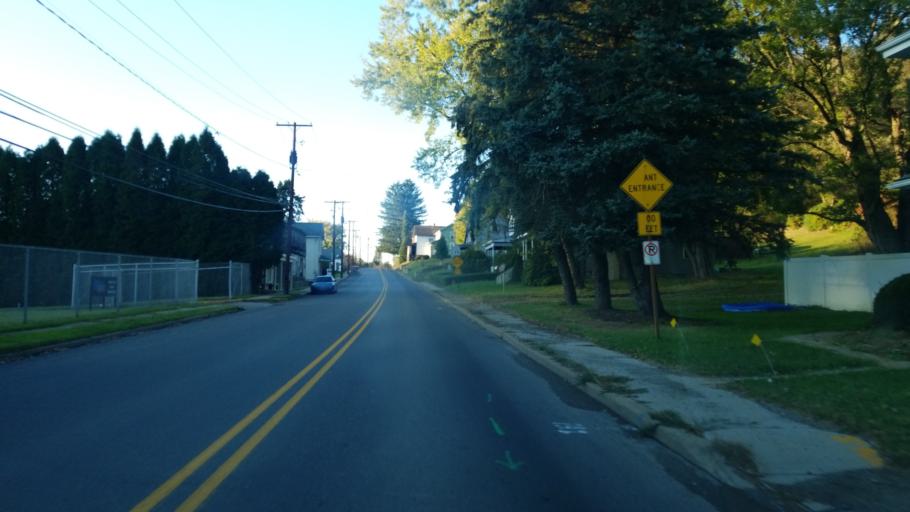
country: US
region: Pennsylvania
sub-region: Jefferson County
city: Punxsutawney
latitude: 40.9545
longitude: -78.9644
